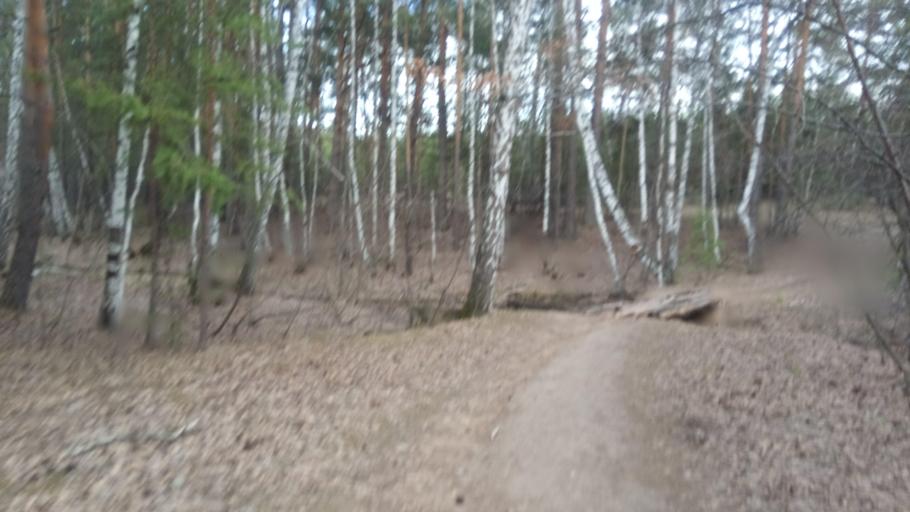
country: RU
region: Chelyabinsk
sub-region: Gorod Chelyabinsk
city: Chelyabinsk
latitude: 55.1406
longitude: 61.3373
